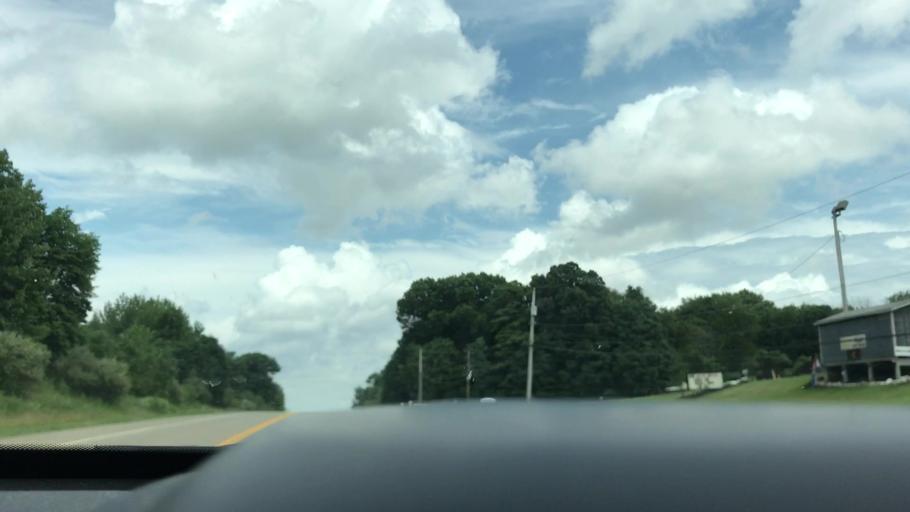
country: US
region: Ohio
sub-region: Stark County
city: Massillon
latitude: 40.7718
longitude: -81.5726
